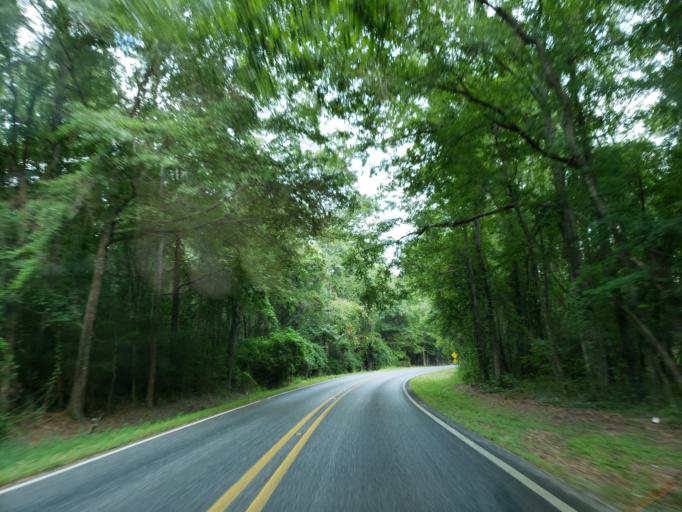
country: US
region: Mississippi
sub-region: Clarke County
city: Stonewall
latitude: 32.1778
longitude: -88.9178
